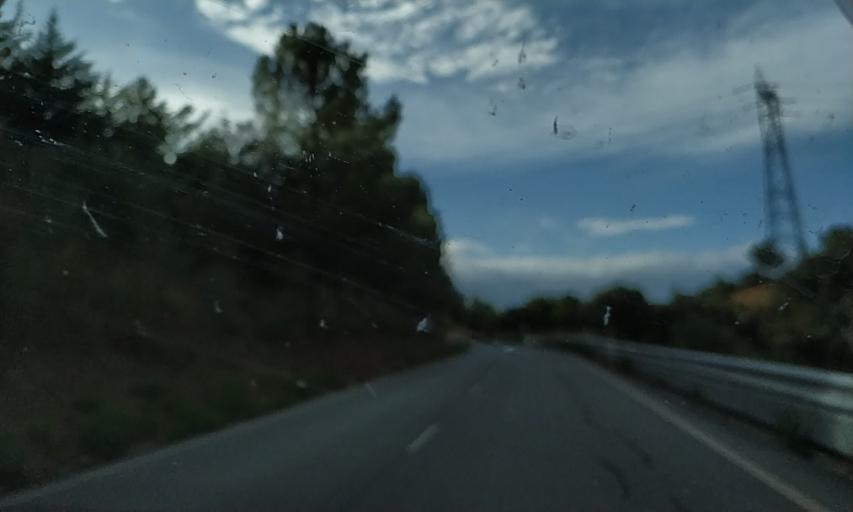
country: PT
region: Viseu
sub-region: Sao Joao da Pesqueira
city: Sao Joao da Pesqueira
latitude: 41.1043
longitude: -7.4601
